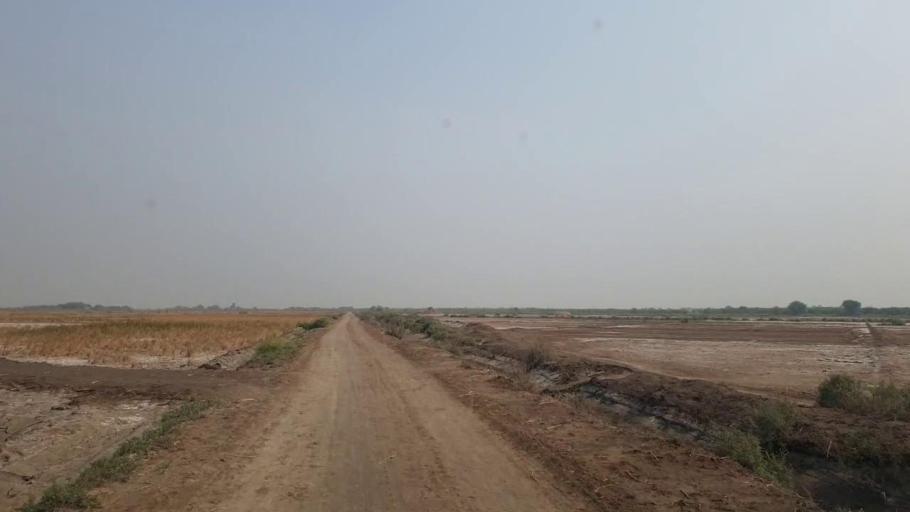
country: PK
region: Sindh
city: Matli
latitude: 25.1175
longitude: 68.6487
